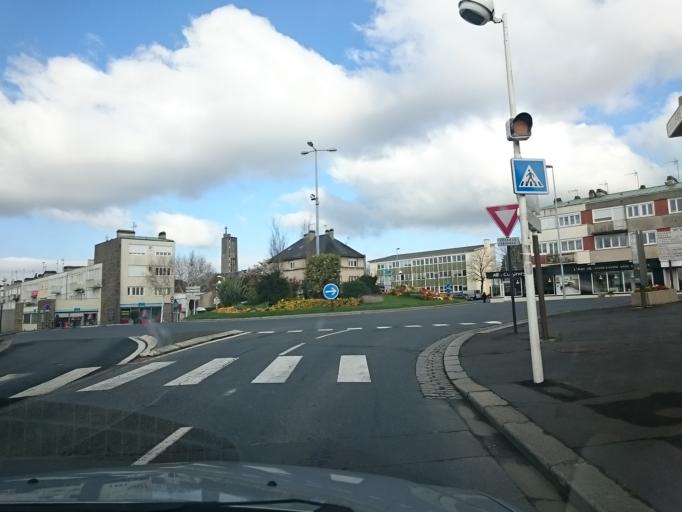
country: FR
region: Lower Normandy
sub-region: Departement de la Manche
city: Saint-Lo
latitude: 49.1152
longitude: -1.0824
